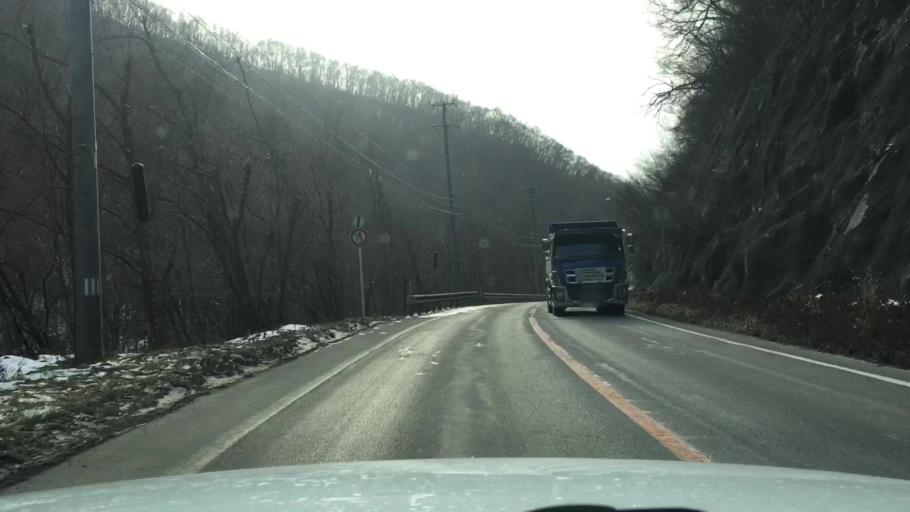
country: JP
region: Iwate
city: Tono
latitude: 39.6298
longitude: 141.5214
